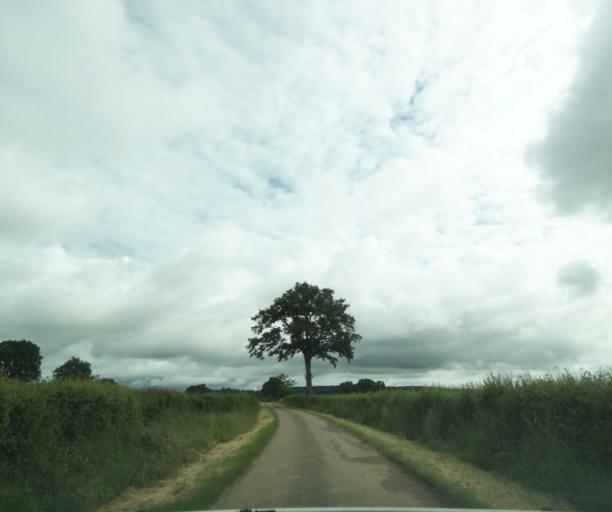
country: FR
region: Bourgogne
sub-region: Departement de Saone-et-Loire
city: Charolles
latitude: 46.4225
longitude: 4.3148
